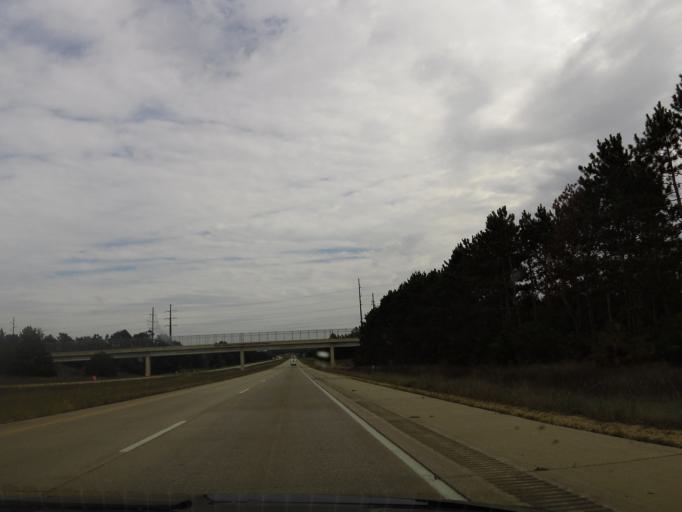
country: US
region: Wisconsin
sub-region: Monroe County
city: Sparta
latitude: 43.9276
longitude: -90.7925
